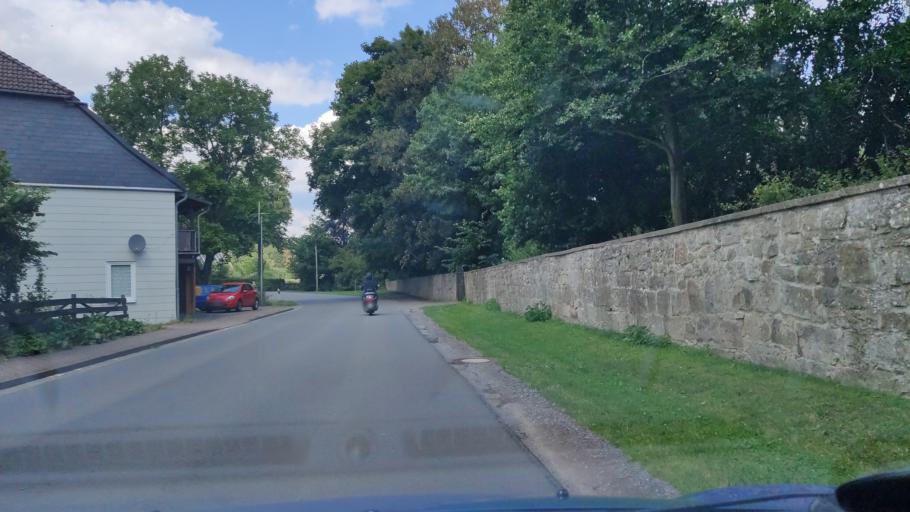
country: DE
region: Lower Saxony
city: Bad Munder am Deister
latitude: 52.1435
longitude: 9.4569
